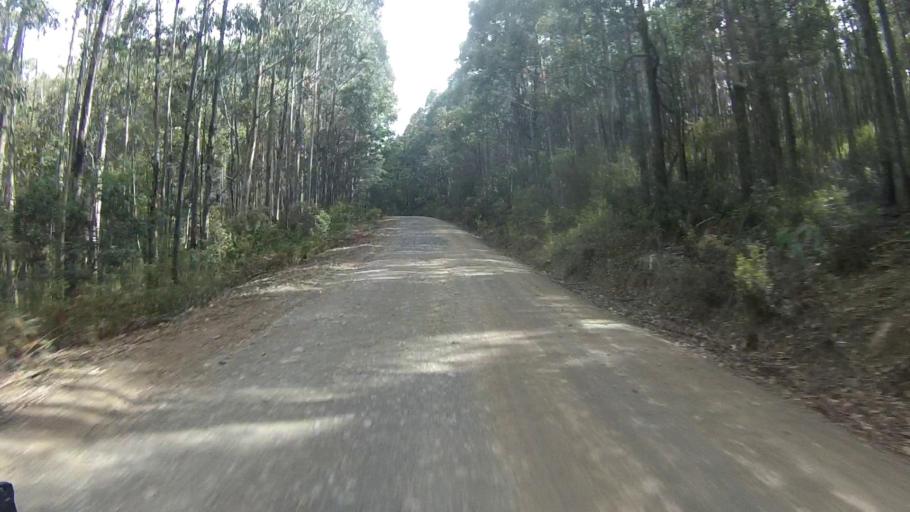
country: AU
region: Tasmania
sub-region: Sorell
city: Sorell
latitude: -42.7480
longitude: 147.8289
